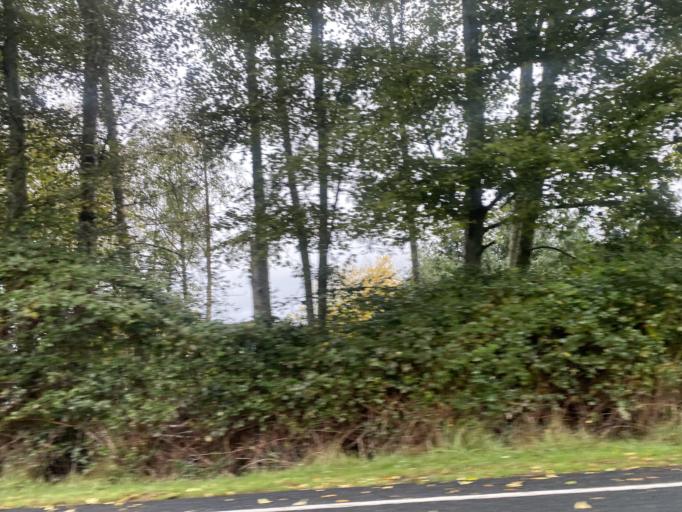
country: US
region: Washington
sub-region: Island County
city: Langley
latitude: 48.0478
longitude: -122.4394
